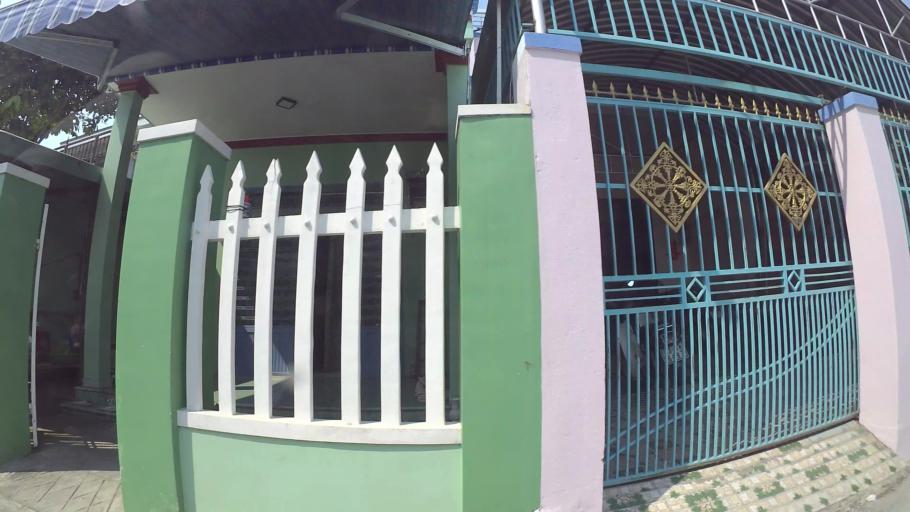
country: VN
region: Da Nang
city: Cam Le
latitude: 16.0127
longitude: 108.2050
